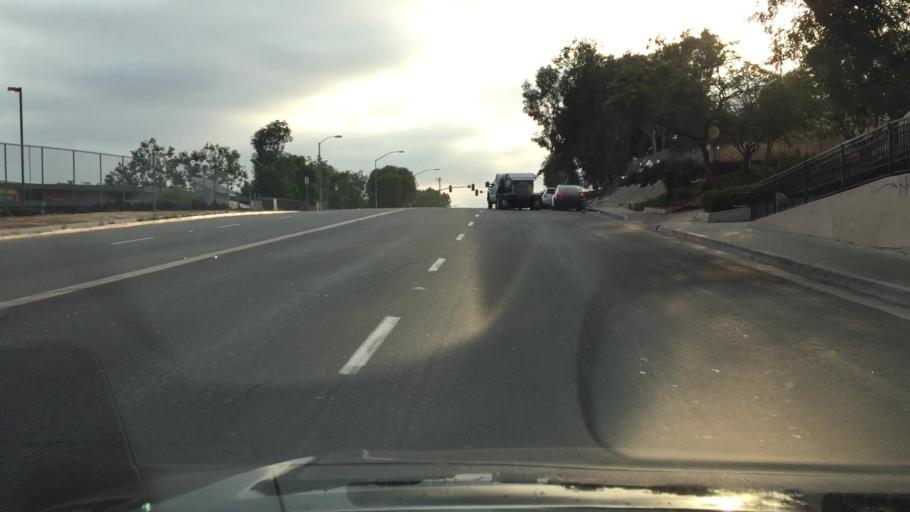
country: US
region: California
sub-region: San Diego County
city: National City
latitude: 32.7115
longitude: -117.0959
